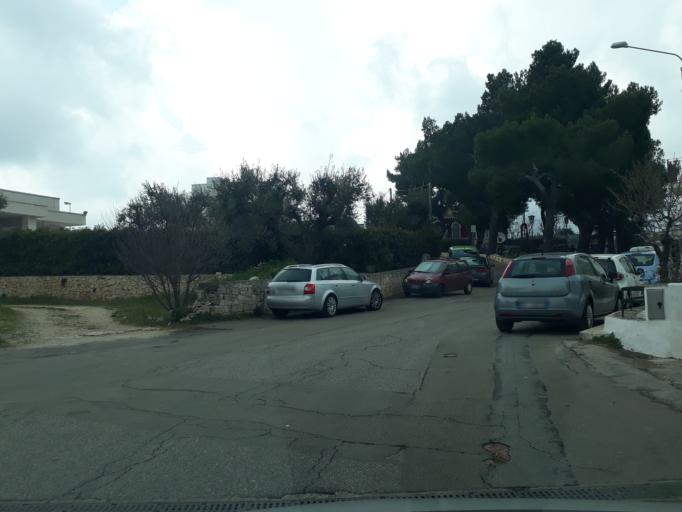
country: IT
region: Apulia
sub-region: Provincia di Brindisi
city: Lamie di Olimpie-Selva
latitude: 40.7915
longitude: 17.3188
